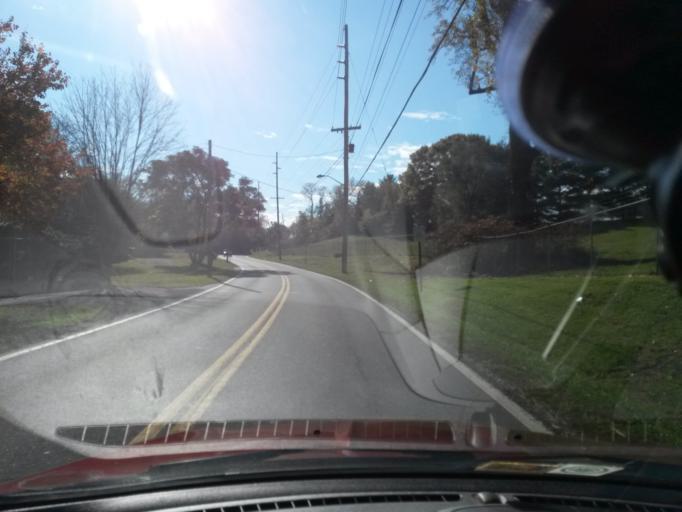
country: US
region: Virginia
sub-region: City of Roanoke
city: Roanoke
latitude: 37.2929
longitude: -79.9256
